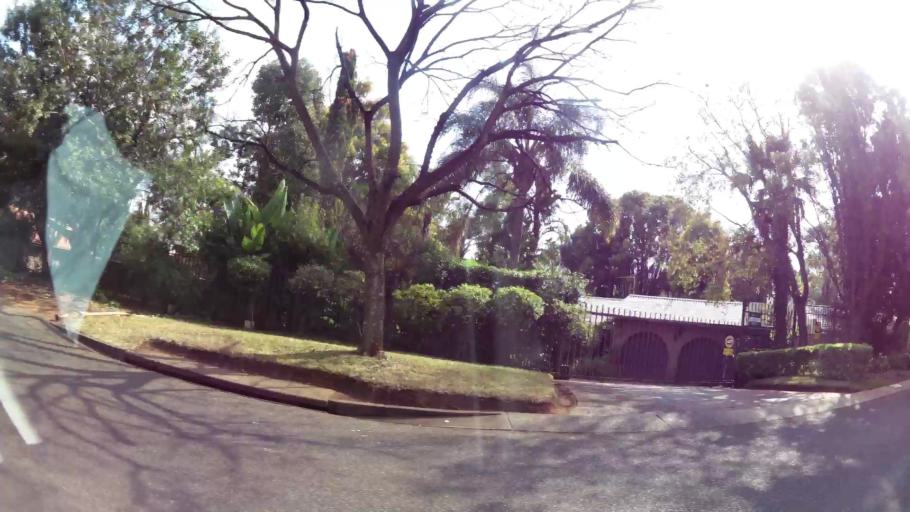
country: ZA
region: Gauteng
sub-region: City of Tshwane Metropolitan Municipality
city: Pretoria
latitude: -25.7815
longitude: 28.3117
